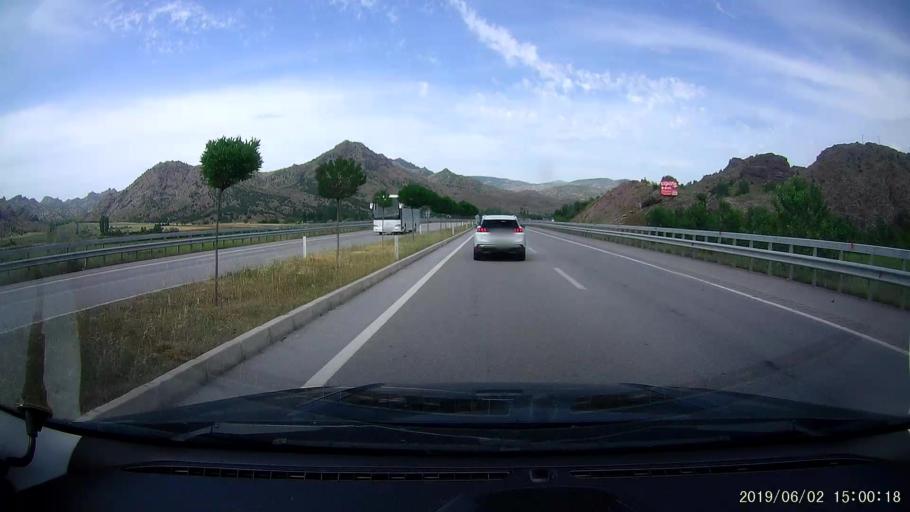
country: TR
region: Corum
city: Osmancik
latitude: 40.9771
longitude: 34.7107
